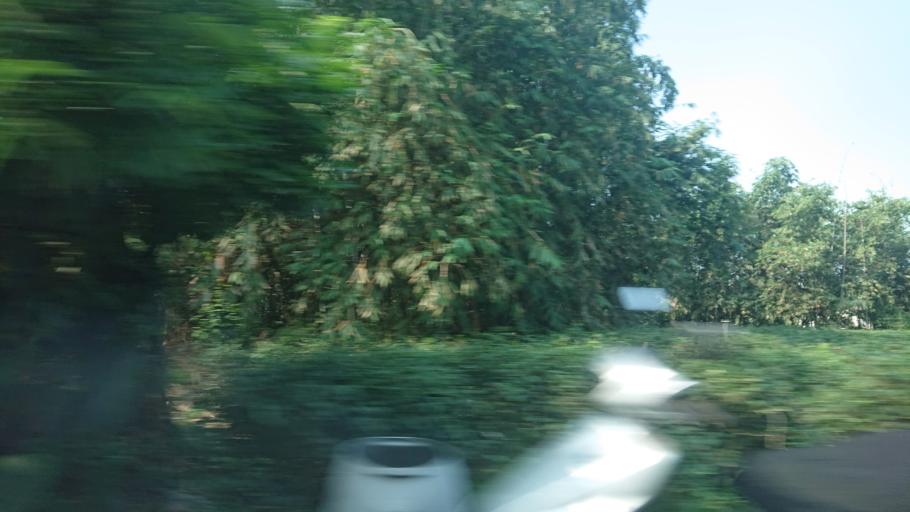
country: TW
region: Taiwan
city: Lugu
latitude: 23.7256
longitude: 120.6675
